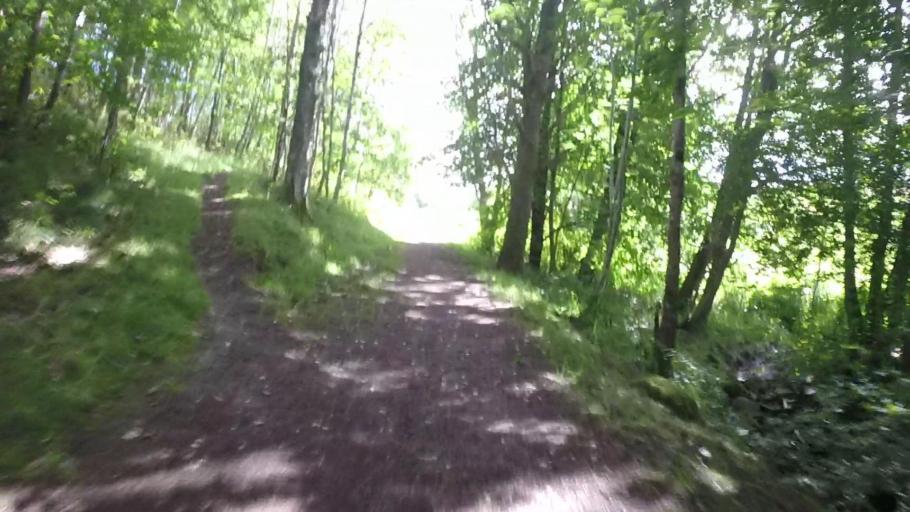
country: SE
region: Vaestra Goetaland
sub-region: Trollhattan
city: Trollhattan
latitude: 58.2519
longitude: 12.2693
